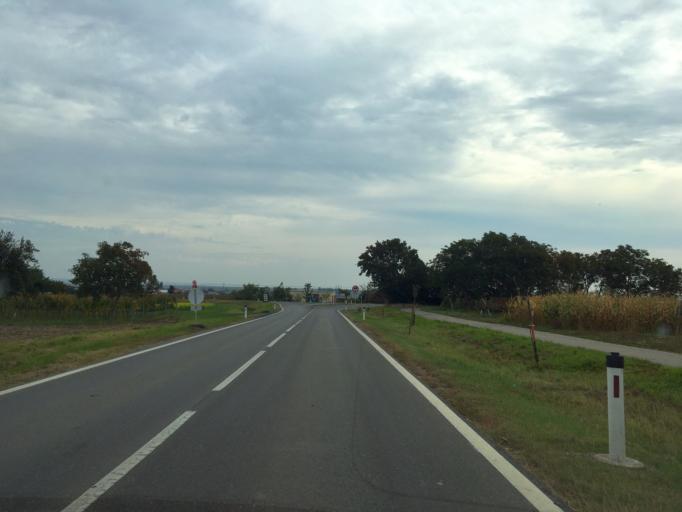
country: AT
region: Burgenland
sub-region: Politischer Bezirk Neusiedl am See
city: Winden am See
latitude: 47.9511
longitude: 16.7439
